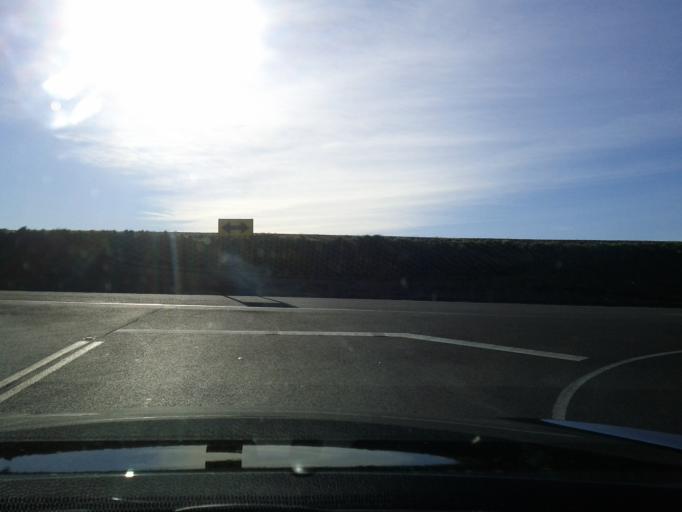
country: US
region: Washington
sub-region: Skagit County
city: Mount Vernon
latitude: 48.4469
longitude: -122.3450
